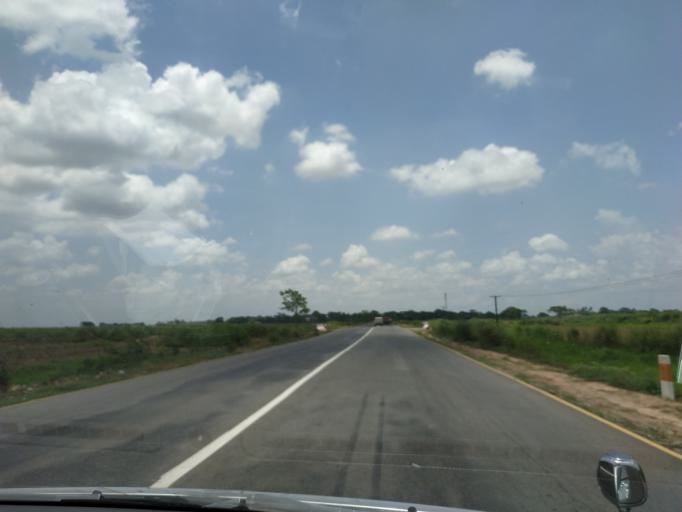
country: MM
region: Bago
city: Bago
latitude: 17.4682
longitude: 96.5727
